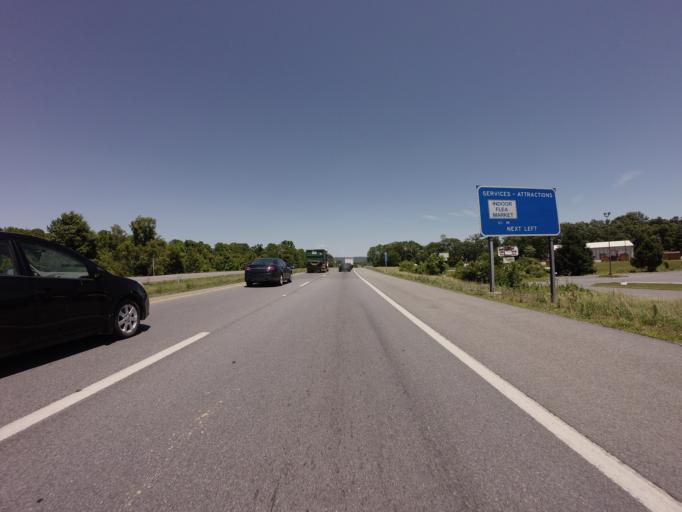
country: US
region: West Virginia
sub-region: Jefferson County
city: Ranson
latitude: 39.3038
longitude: -77.8149
